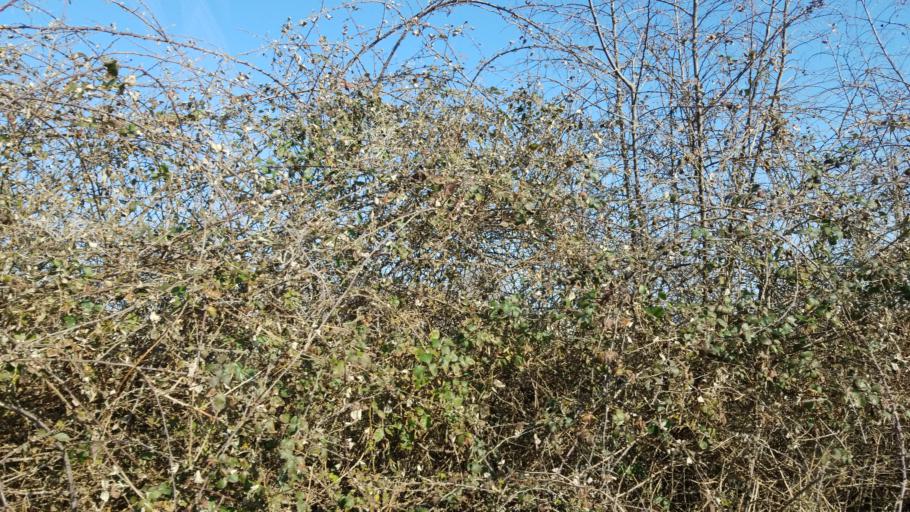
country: AL
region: Shkoder
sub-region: Rrethi i Shkodres
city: Velipoje
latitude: 41.8711
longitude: 19.4115
